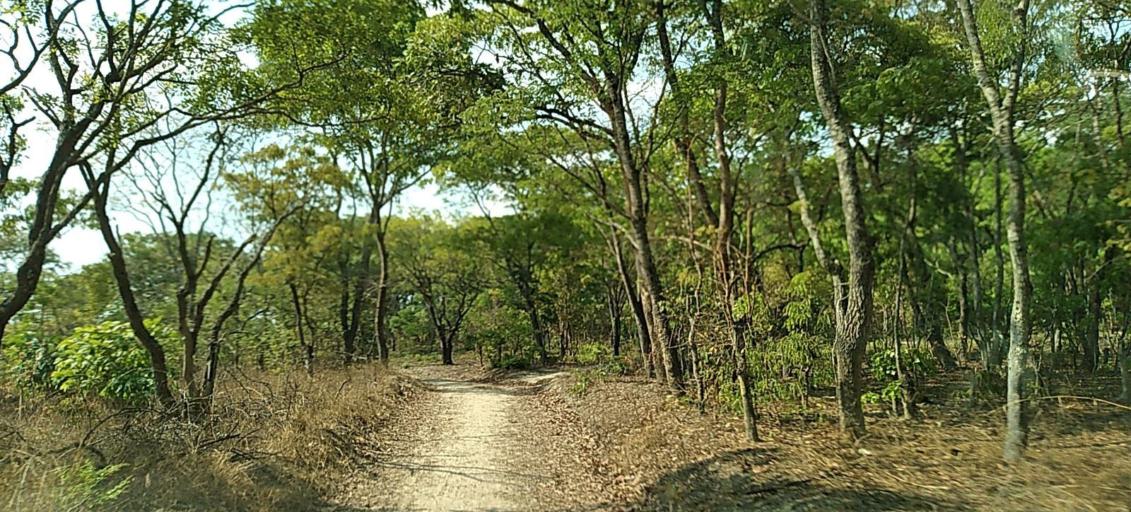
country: ZM
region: Copperbelt
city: Luanshya
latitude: -13.2253
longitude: 28.3330
